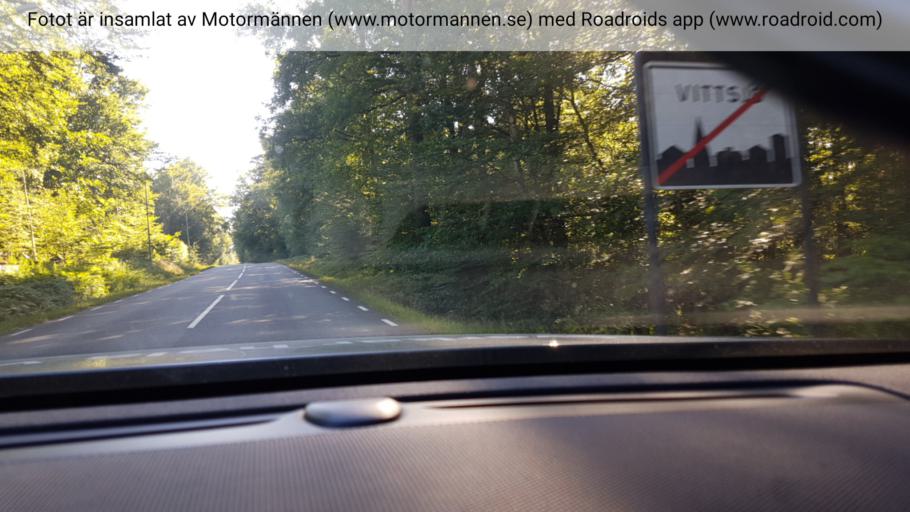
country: SE
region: Skane
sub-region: Hassleholms Kommun
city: Bjarnum
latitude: 56.3347
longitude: 13.6761
